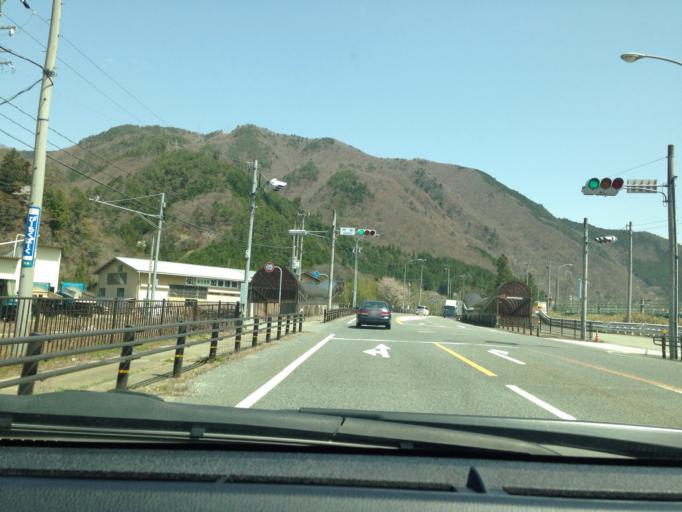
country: JP
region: Gifu
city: Takayama
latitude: 35.9696
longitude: 137.2608
